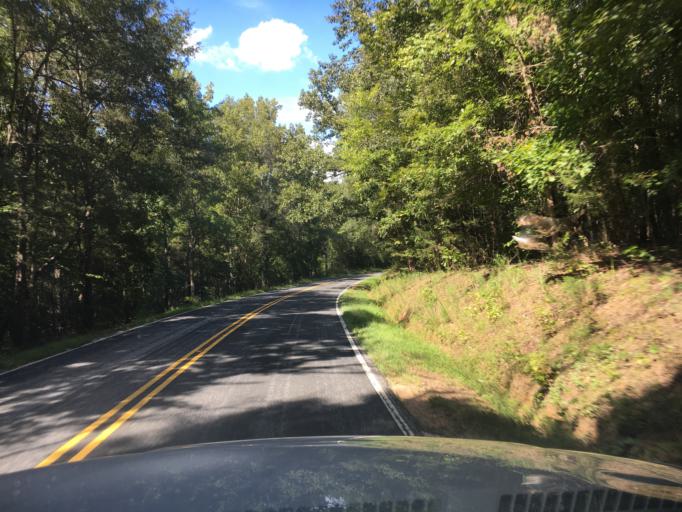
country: US
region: South Carolina
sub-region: Greenwood County
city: Ware Shoals
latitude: 34.4304
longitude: -82.2689
